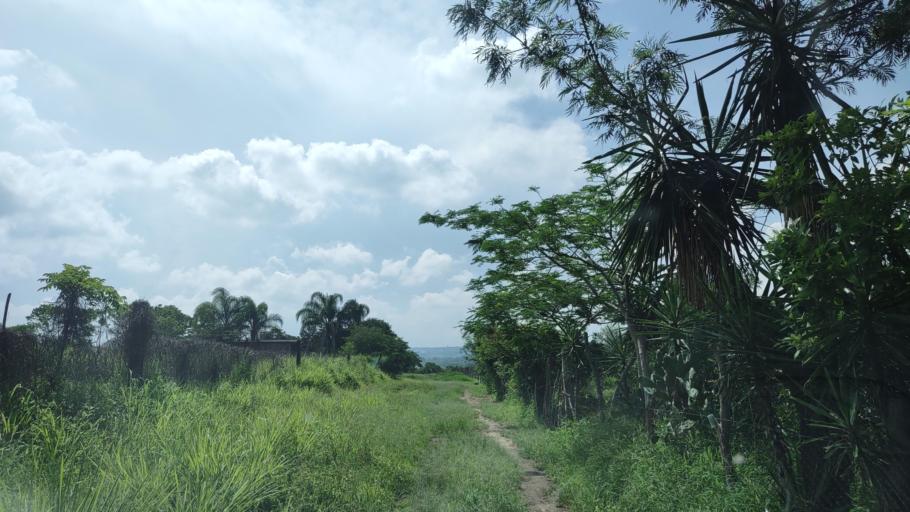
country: MX
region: Veracruz
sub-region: Emiliano Zapata
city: Dos Rios
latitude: 19.4301
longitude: -96.8072
